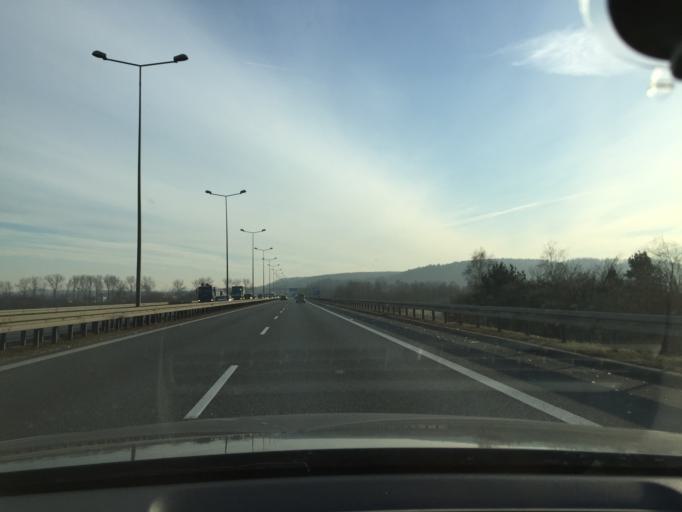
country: PL
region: Lesser Poland Voivodeship
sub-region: Powiat krakowski
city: Piekary
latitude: 50.0271
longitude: 19.8221
